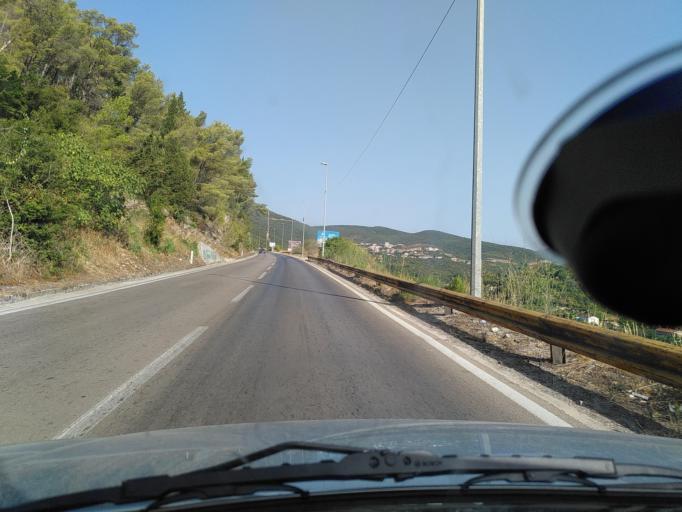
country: ME
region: Ulcinj
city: Ulcinj
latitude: 41.9458
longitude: 19.2051
